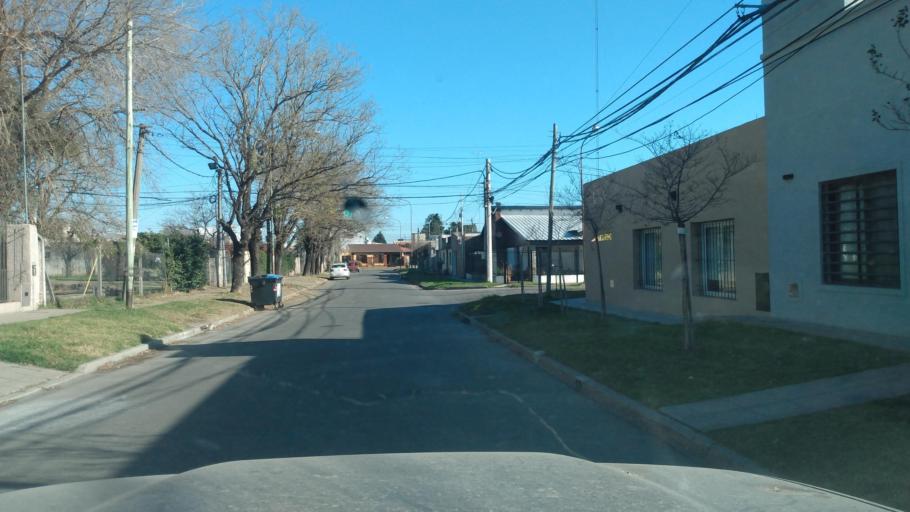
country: AR
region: Buenos Aires
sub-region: Partido de Lujan
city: Lujan
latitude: -34.5622
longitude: -59.1001
